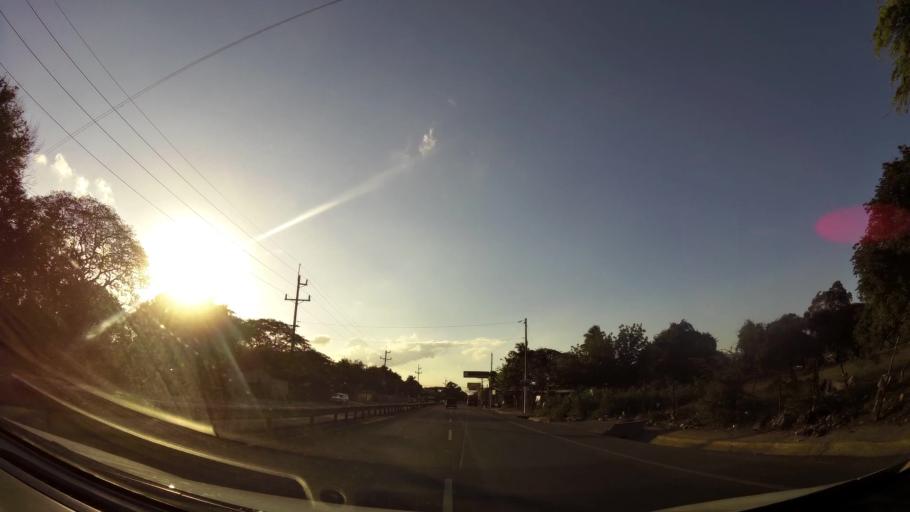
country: DO
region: Santiago
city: Palmar Arriba
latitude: 19.5041
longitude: -70.7505
